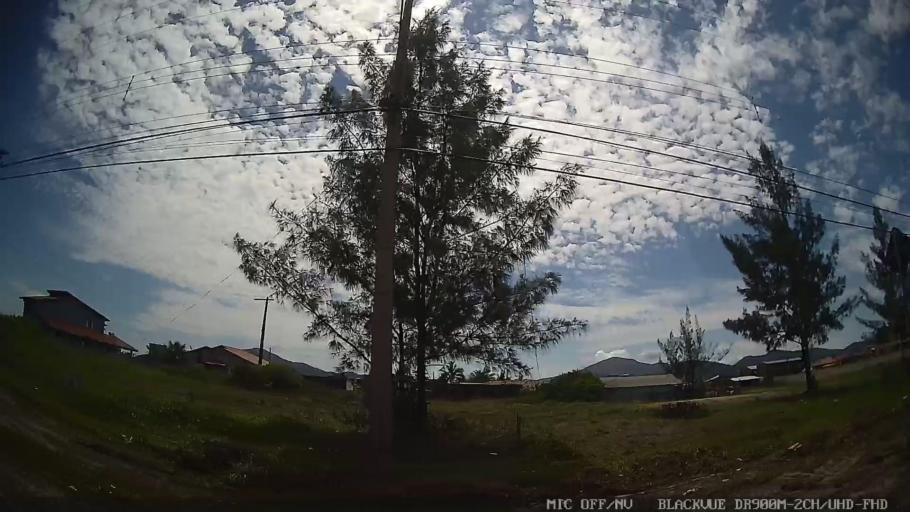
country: BR
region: Sao Paulo
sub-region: Iguape
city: Iguape
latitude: -24.7238
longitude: -47.5061
